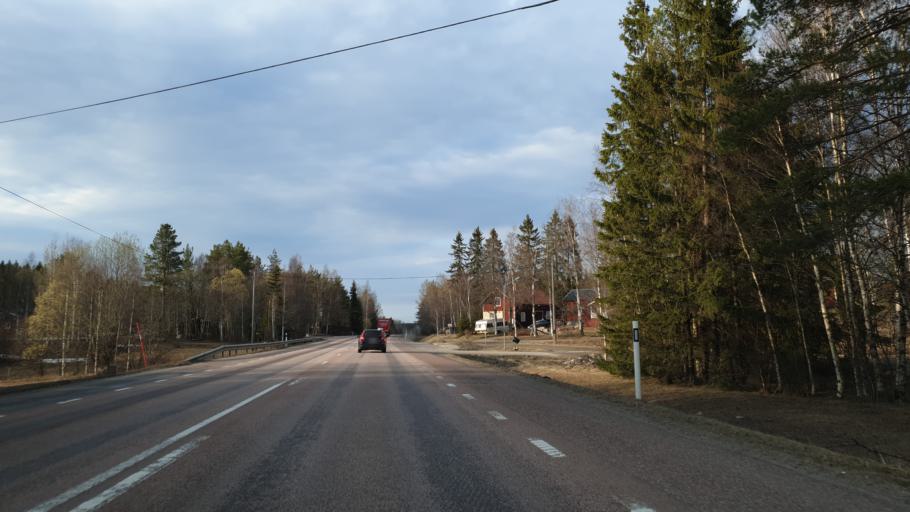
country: SE
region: Gaevleborg
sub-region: Nordanstigs Kommun
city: Bergsjoe
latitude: 61.9567
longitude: 17.2408
